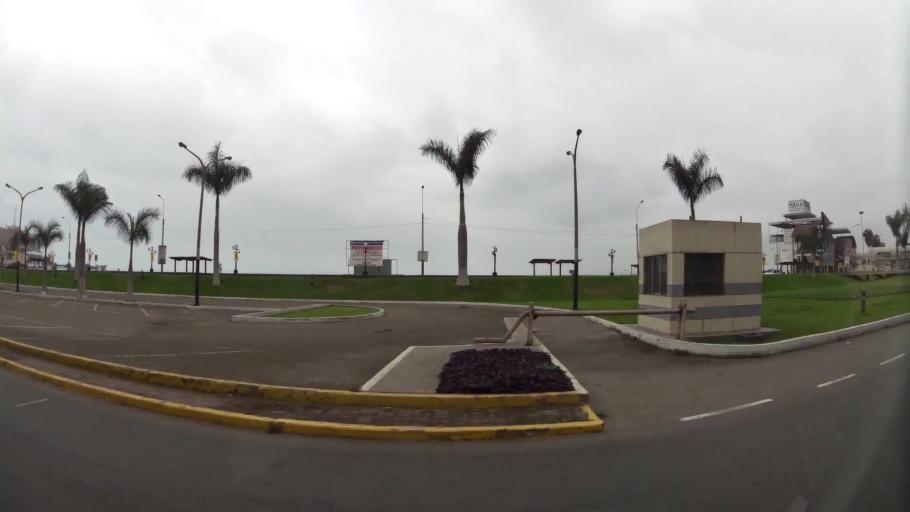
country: PE
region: Lima
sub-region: Lima
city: Surco
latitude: -12.1650
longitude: -77.0264
